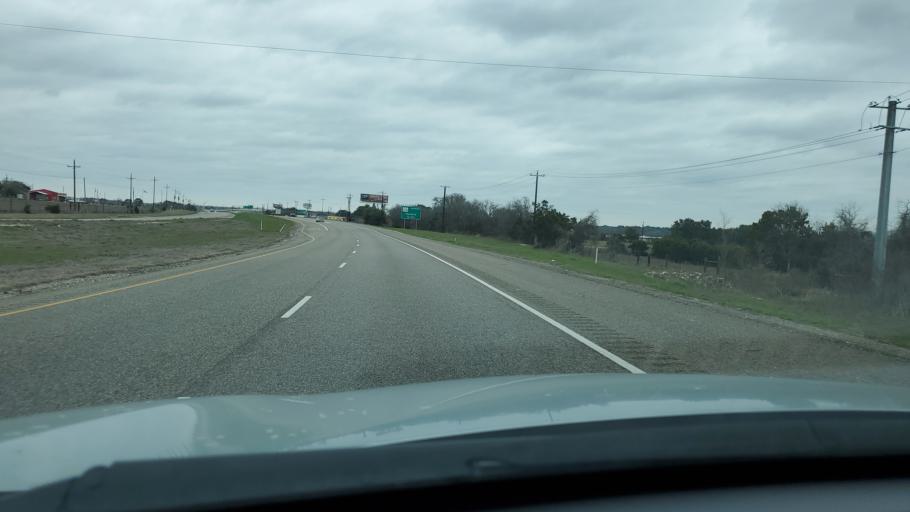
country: US
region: Texas
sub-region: Williamson County
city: Florence
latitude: 30.8111
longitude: -97.7726
